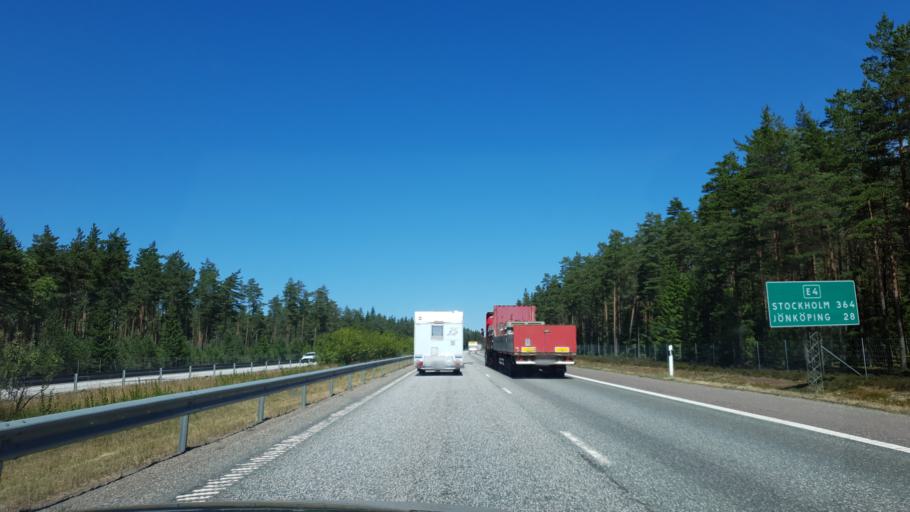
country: SE
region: Joenkoeping
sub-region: Vaggeryds Kommun
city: Vaggeryd
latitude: 57.5388
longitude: 14.1254
